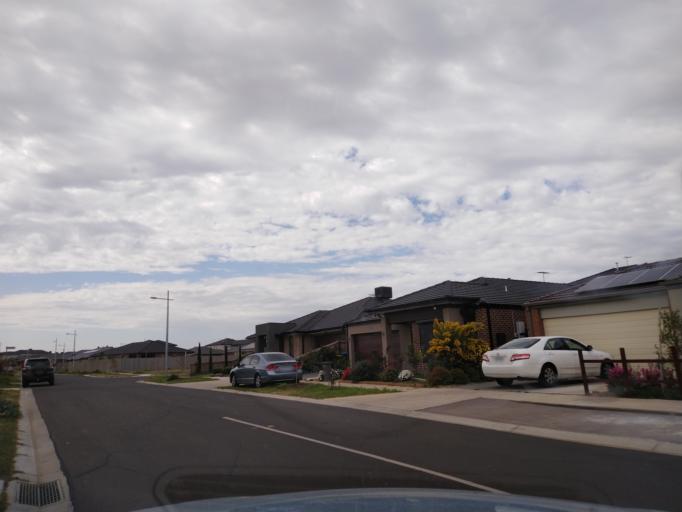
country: AU
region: Victoria
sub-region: Wyndham
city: Williams Landing
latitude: -37.8411
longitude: 144.7128
